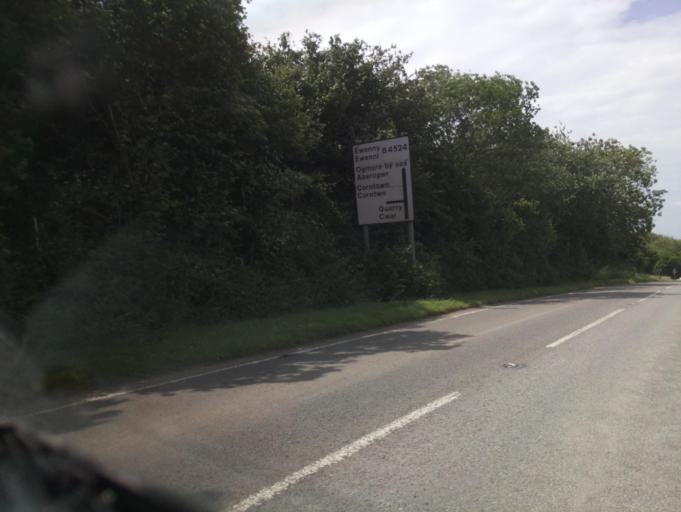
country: GB
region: Wales
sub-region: Bridgend county borough
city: Coity
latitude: 51.4841
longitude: -3.5439
